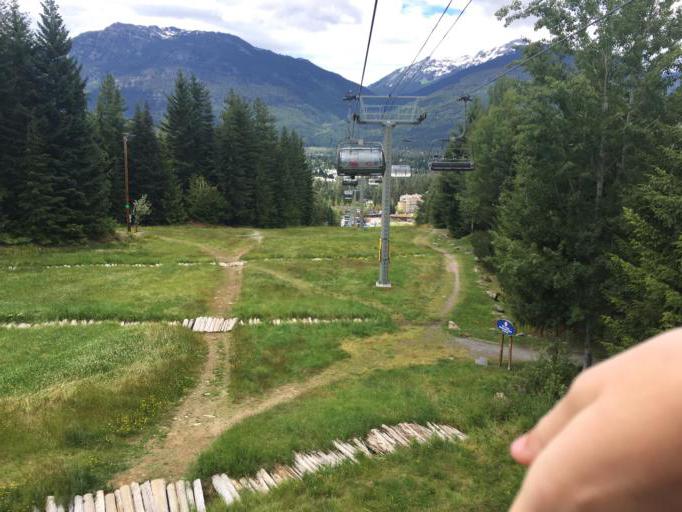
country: CA
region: British Columbia
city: Whistler
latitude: 50.1131
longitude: -122.9408
